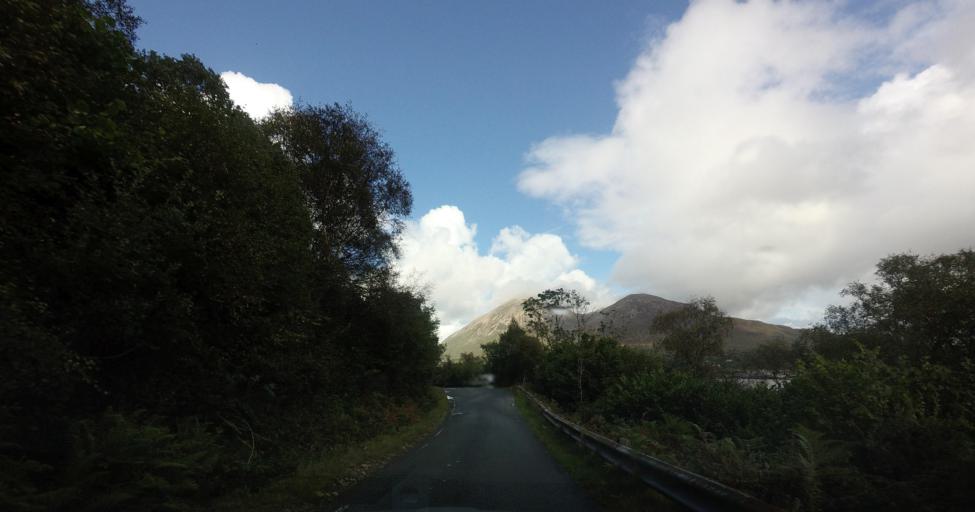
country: GB
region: Scotland
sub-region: Highland
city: Portree
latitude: 57.2003
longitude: -6.0274
